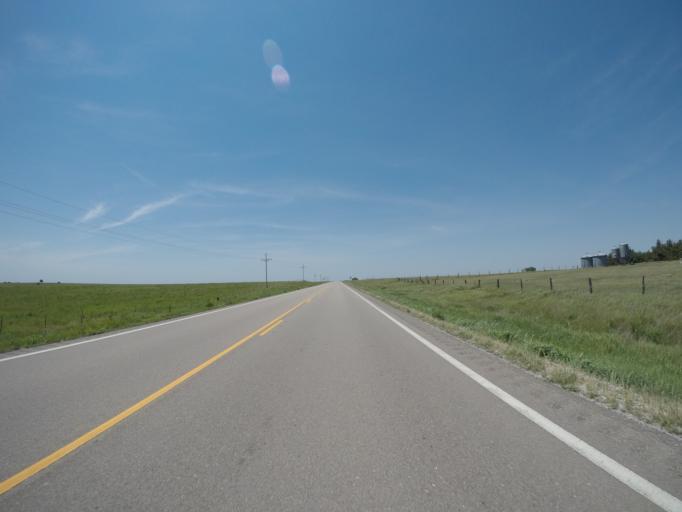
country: US
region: Kansas
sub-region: Dickinson County
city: Solomon
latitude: 39.0308
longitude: -97.3184
